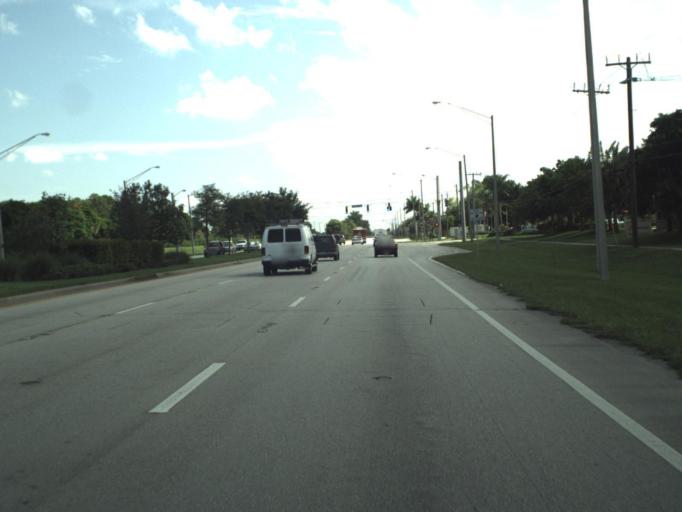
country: US
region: Florida
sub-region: Palm Beach County
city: Royal Palm Beach
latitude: 26.7008
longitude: -80.2014
